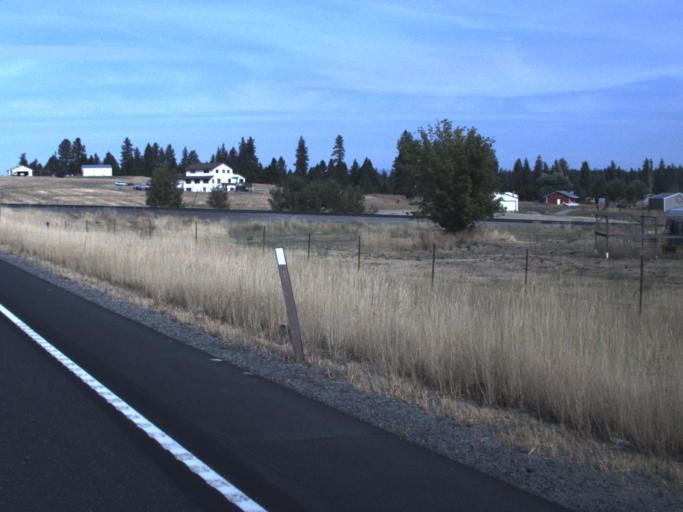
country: US
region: Washington
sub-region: Spokane County
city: Deer Park
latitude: 47.9027
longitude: -117.4388
